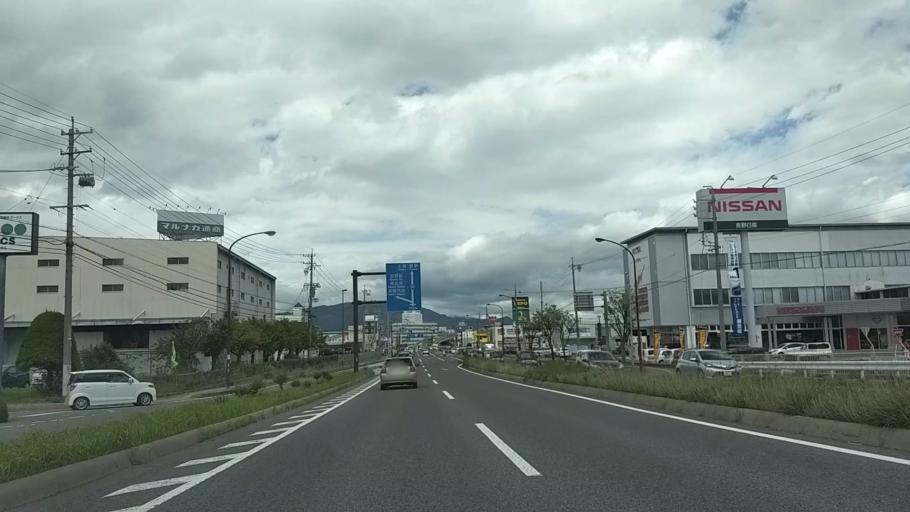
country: JP
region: Nagano
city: Nagano-shi
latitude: 36.6238
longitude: 138.2000
